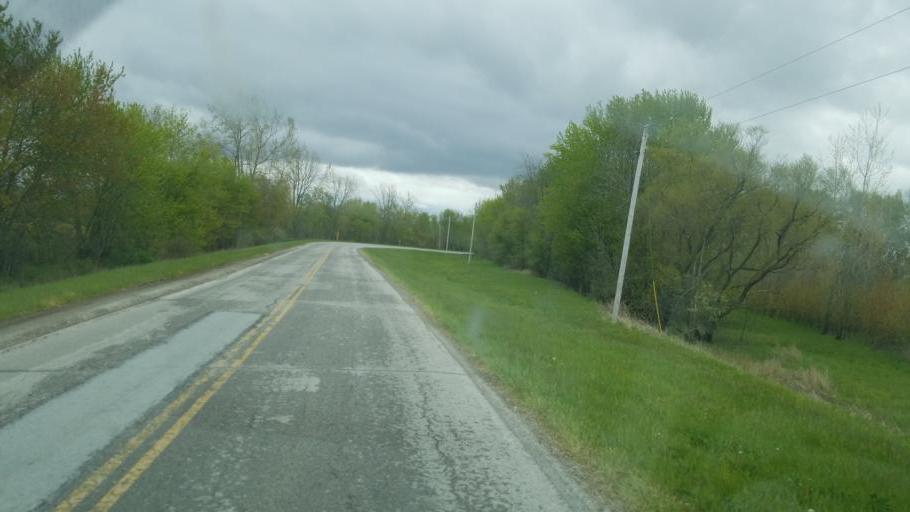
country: US
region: Ohio
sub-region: Marion County
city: Marion
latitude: 40.5622
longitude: -83.2559
